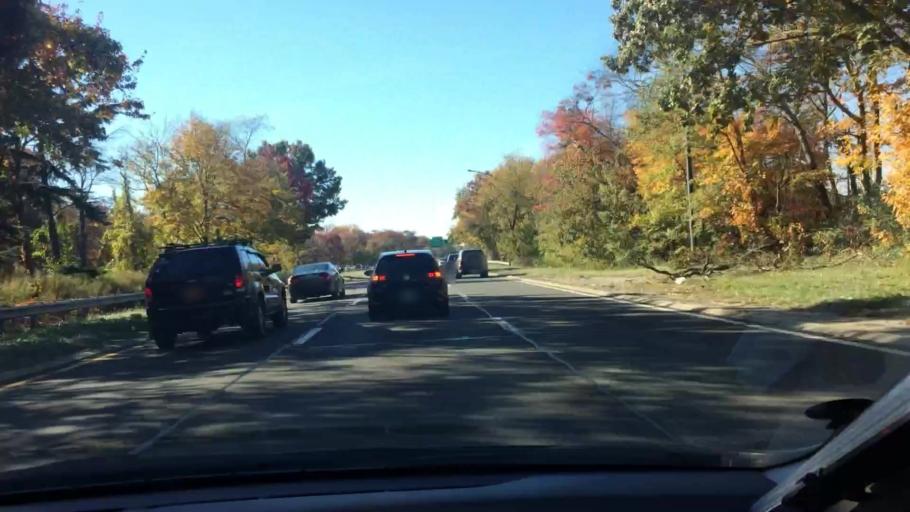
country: US
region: New York
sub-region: Nassau County
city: South Farmingdale
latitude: 40.7053
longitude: -73.4422
